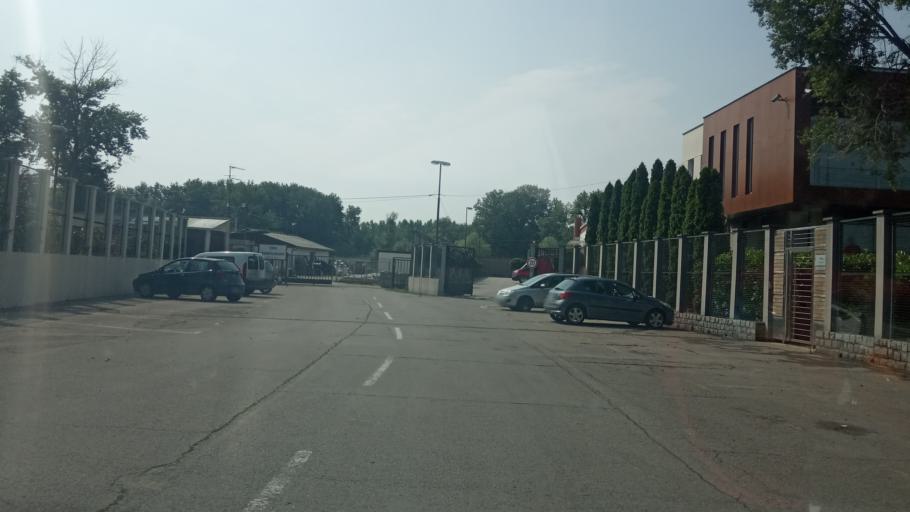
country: RS
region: Central Serbia
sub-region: Belgrade
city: Palilula
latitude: 44.8452
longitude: 20.5143
